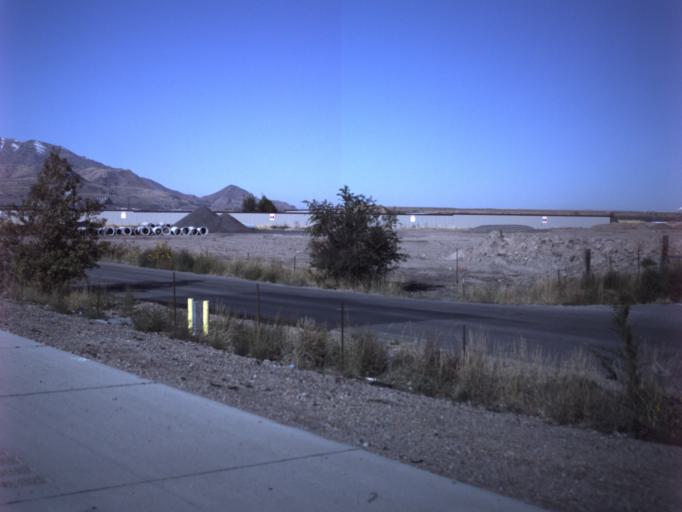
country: US
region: Utah
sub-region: Salt Lake County
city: Magna
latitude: 40.7213
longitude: -112.0489
